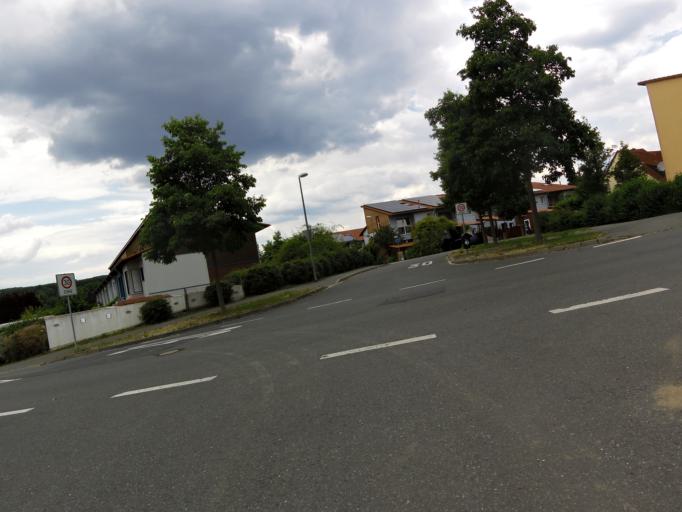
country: DE
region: Bavaria
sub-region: Regierungsbezirk Unterfranken
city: Eibelstadt
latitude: 49.7225
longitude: 9.9622
